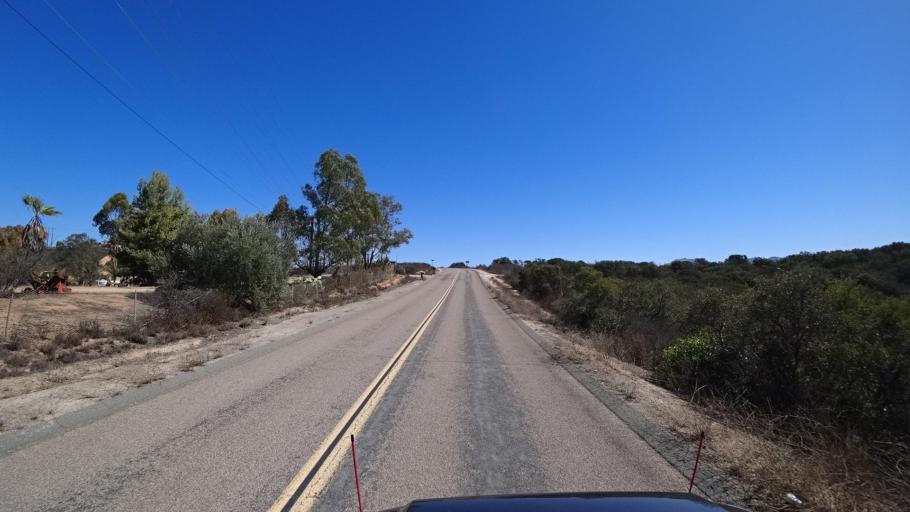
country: US
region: California
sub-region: San Diego County
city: Harbison Canyon
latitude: 32.7961
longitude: -116.7963
